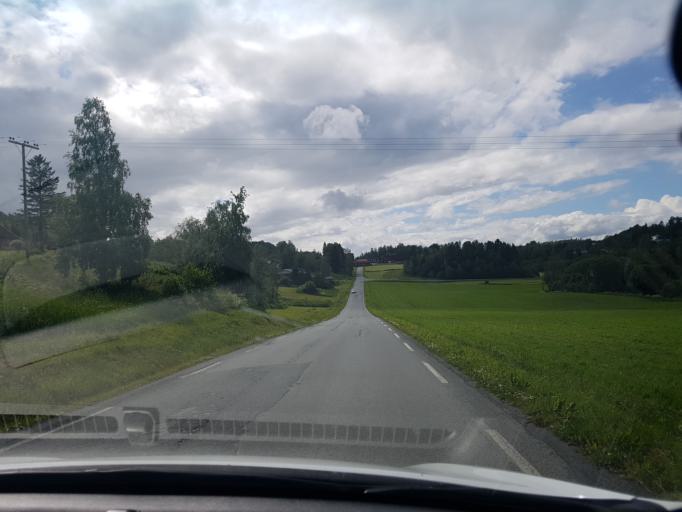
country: NO
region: Nord-Trondelag
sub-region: Stjordal
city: Stjordalshalsen
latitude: 63.5960
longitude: 10.9779
